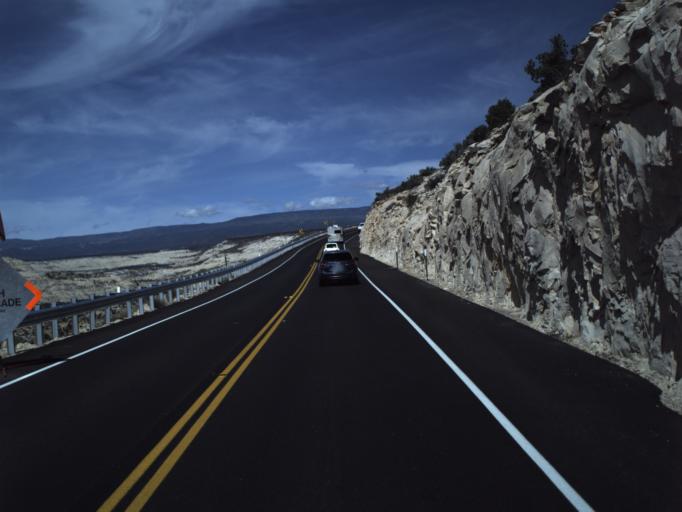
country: US
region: Utah
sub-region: Wayne County
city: Loa
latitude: 37.8178
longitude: -111.4113
